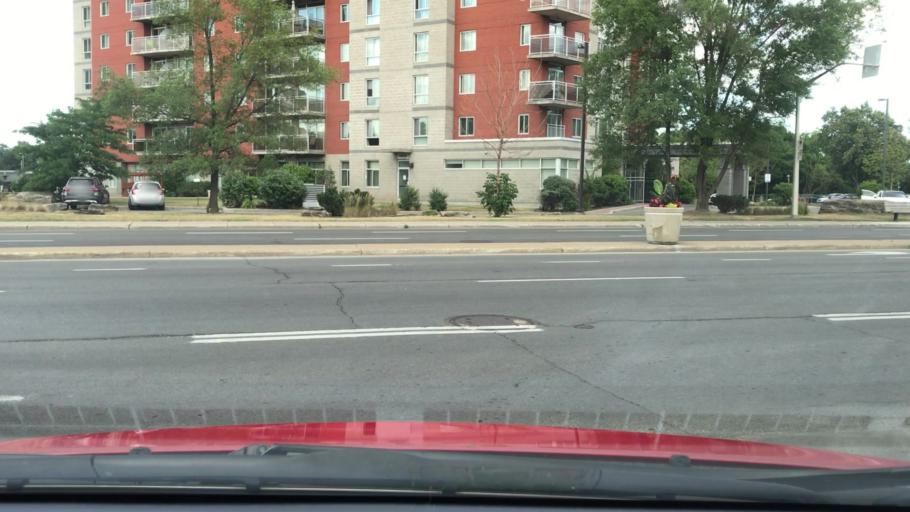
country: CA
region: Quebec
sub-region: Laval
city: Laval
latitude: 45.5495
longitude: -73.7441
